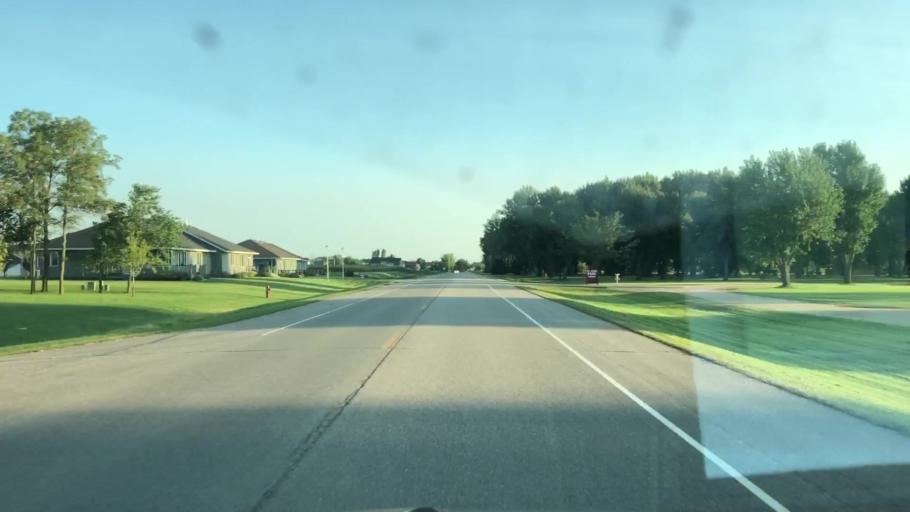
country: US
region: Minnesota
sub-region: Nobles County
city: Worthington
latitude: 43.6058
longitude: -95.6367
